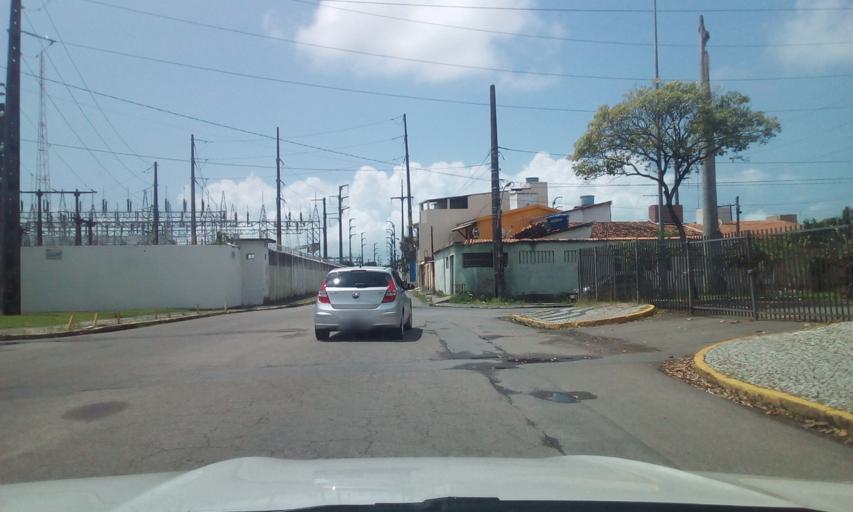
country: BR
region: Pernambuco
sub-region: Recife
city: Recife
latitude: -8.0642
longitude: -34.9296
